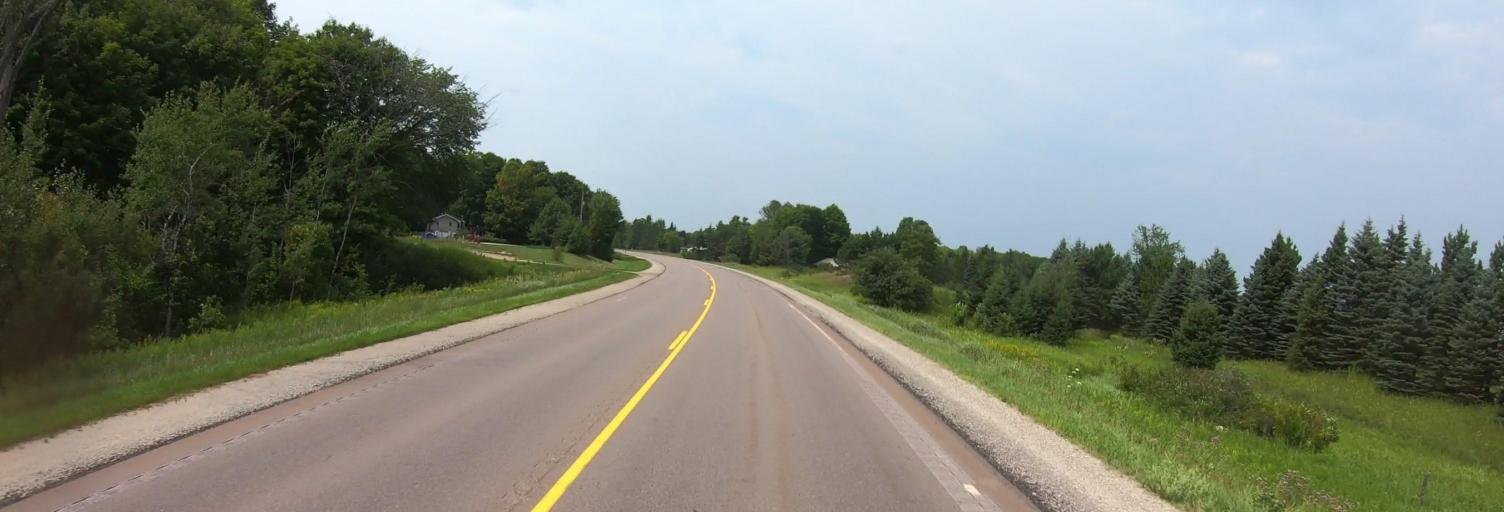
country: US
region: Michigan
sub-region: Alger County
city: Munising
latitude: 46.3519
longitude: -86.9534
